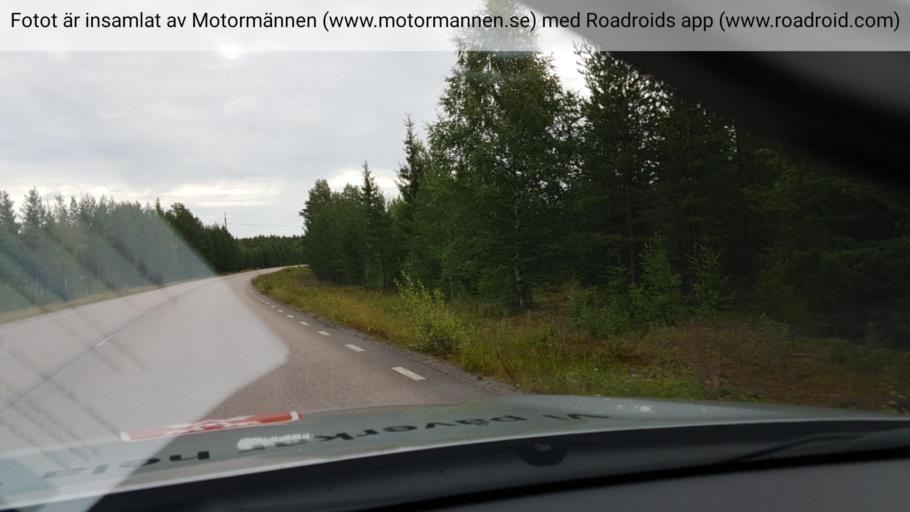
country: SE
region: Norrbotten
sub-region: Bodens Kommun
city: Boden
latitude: 65.8197
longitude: 21.5910
